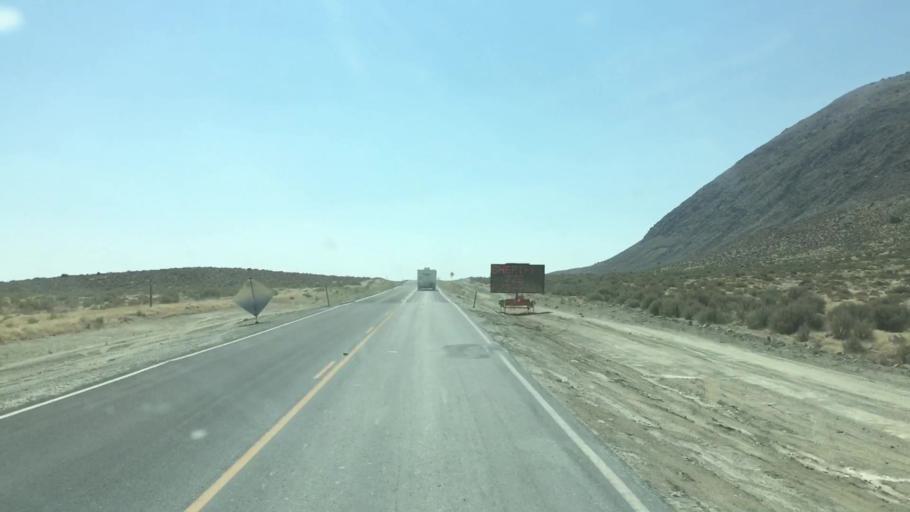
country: US
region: Nevada
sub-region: Pershing County
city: Lovelock
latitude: 40.7502
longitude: -119.2851
